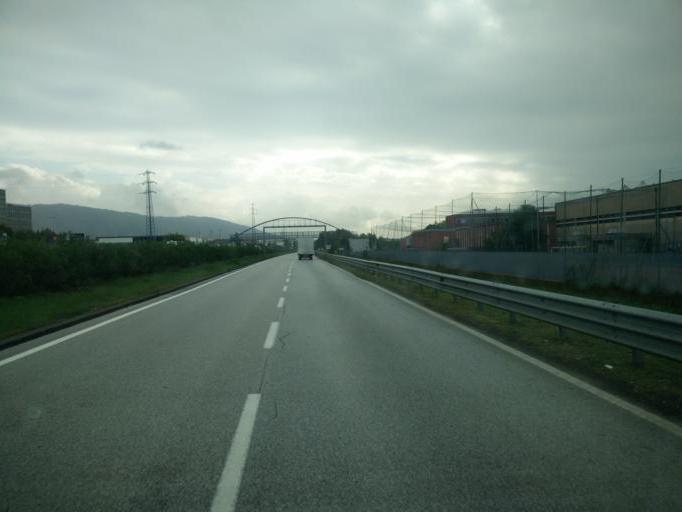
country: IT
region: Tuscany
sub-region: Provincia di Prato
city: Prato
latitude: 43.8775
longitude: 11.0699
